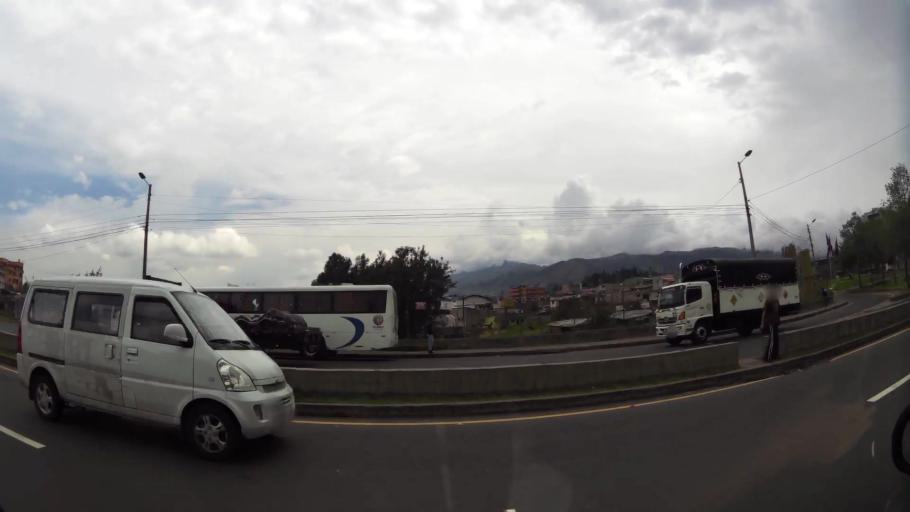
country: EC
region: Pichincha
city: Quito
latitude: -0.2902
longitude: -78.5370
